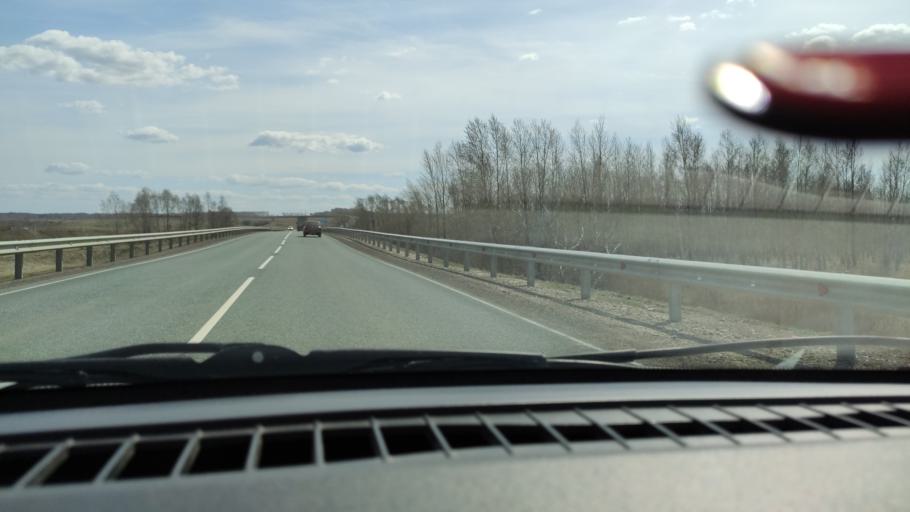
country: RU
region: Bashkortostan
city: Kushnarenkovo
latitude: 55.1488
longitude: 55.1485
